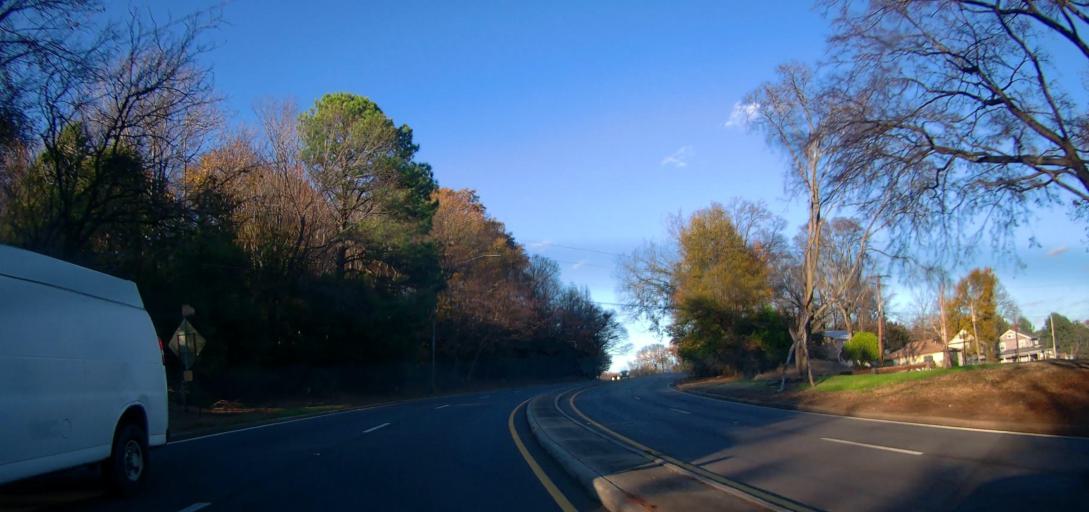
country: US
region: Alabama
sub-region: Jefferson County
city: Birmingham
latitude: 33.5585
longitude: -86.8207
